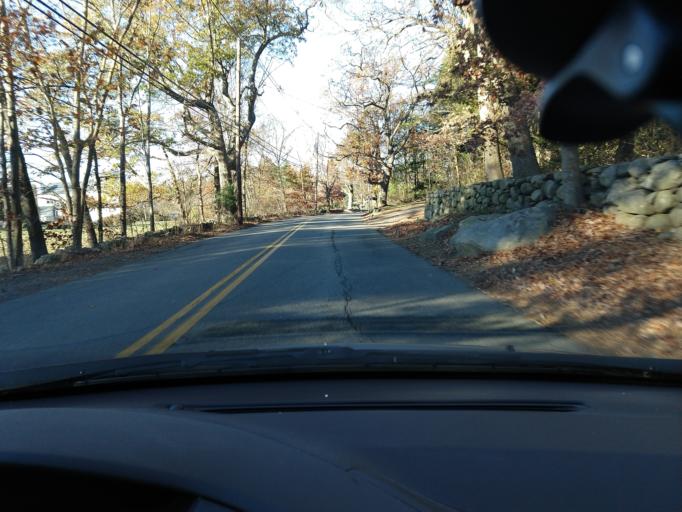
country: US
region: Massachusetts
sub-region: Middlesex County
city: Concord
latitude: 42.4924
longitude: -71.3328
